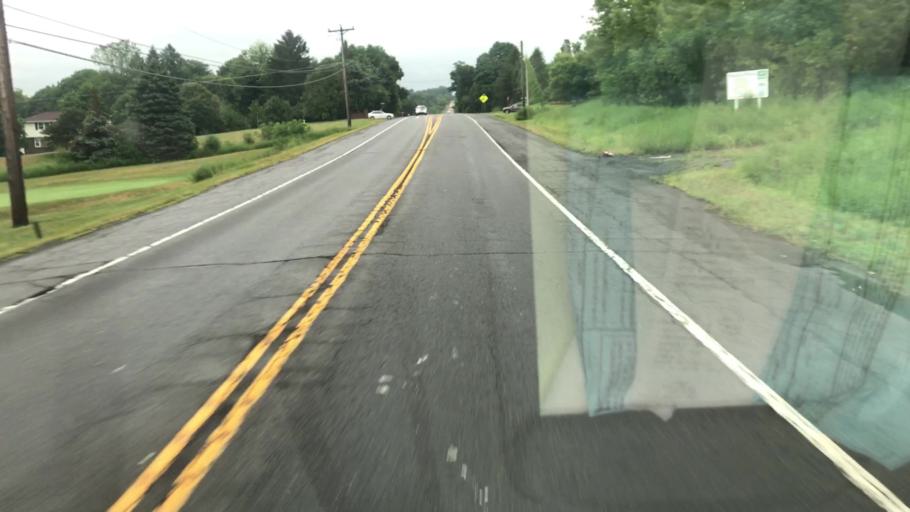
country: US
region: New York
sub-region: Onondaga County
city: Fayetteville
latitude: 43.0236
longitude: -76.0342
